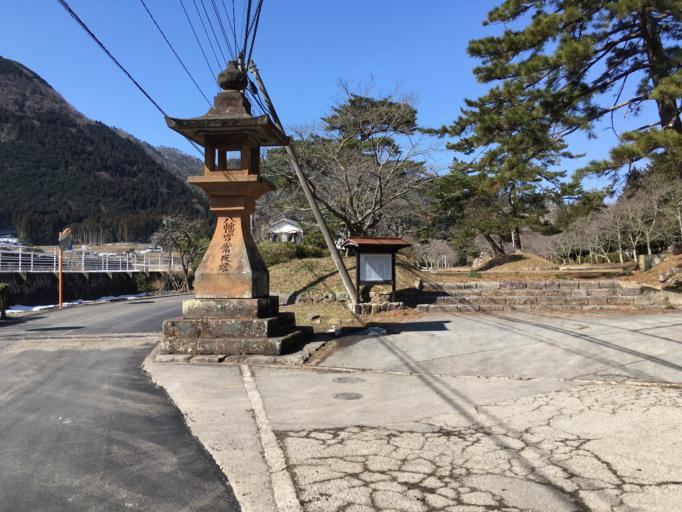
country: JP
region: Shimane
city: Masuda
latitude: 34.4528
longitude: 131.7582
